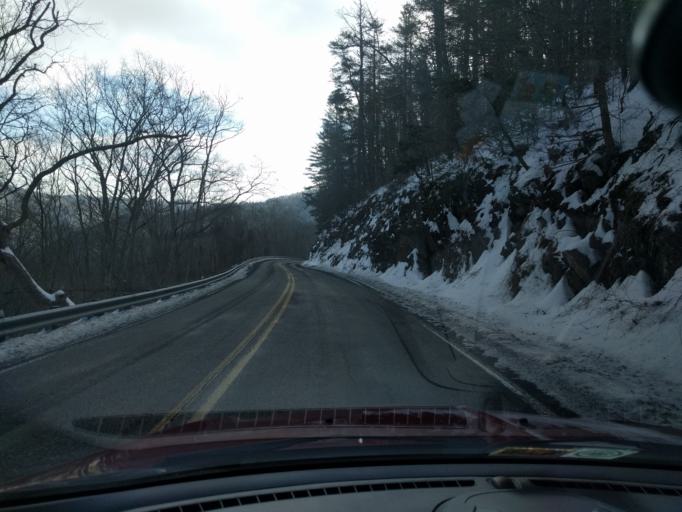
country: US
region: Virginia
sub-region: Bath County
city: Warm Springs
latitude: 38.1231
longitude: -79.9431
